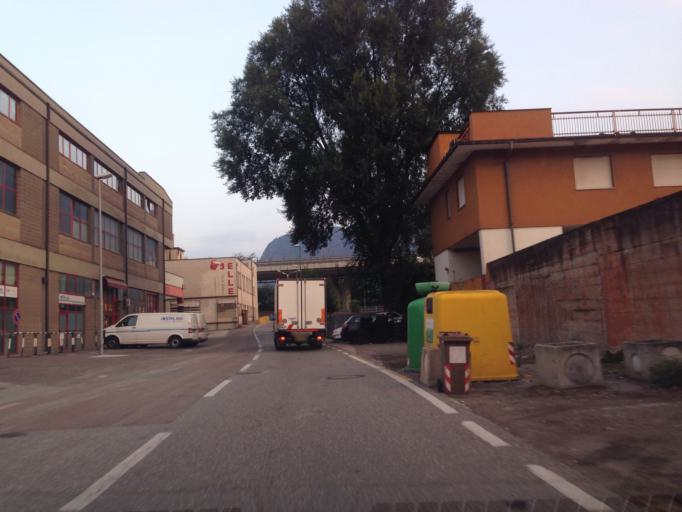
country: IT
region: Trentino-Alto Adige
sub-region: Bolzano
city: Bolzano
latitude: 46.4837
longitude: 11.3298
